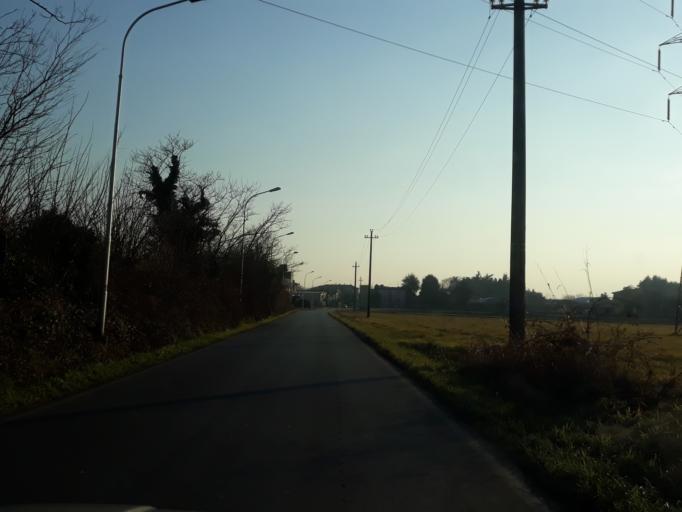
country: IT
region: Lombardy
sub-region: Provincia di Monza e Brianza
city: Bellusco
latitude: 45.6281
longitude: 9.4184
